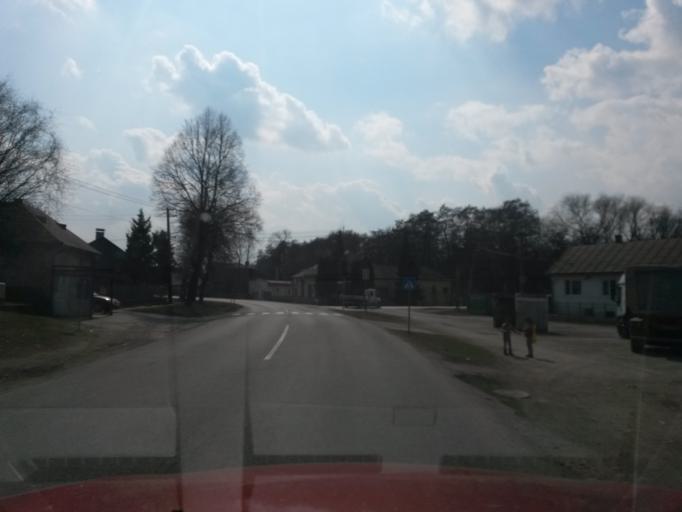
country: SK
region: Kosicky
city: Kosice
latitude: 48.5997
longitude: 21.1688
